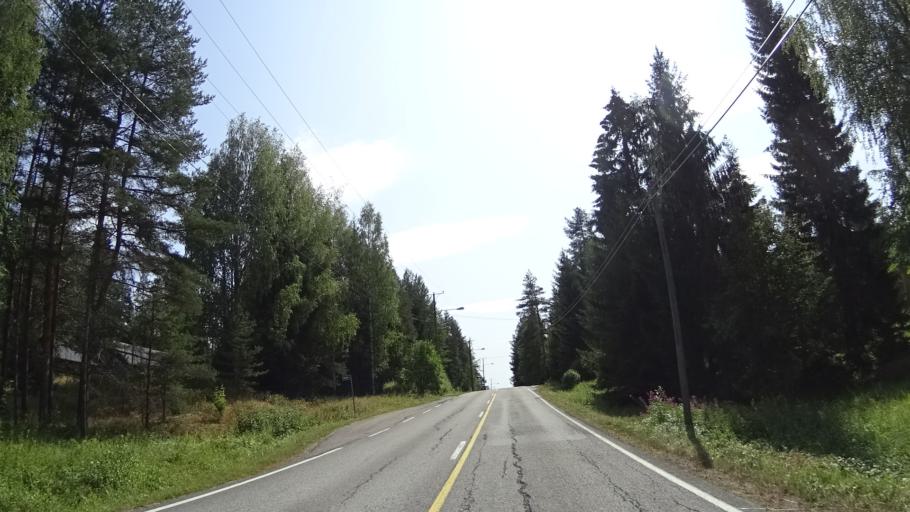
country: FI
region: Pirkanmaa
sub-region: Ylae-Pirkanmaa
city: Maenttae
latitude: 61.9025
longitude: 24.7903
